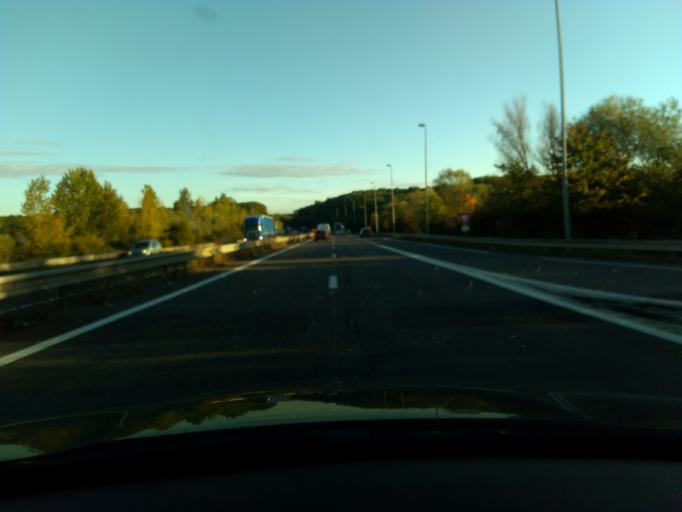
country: FR
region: Lorraine
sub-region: Departement de la Moselle
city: Peltre
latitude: 49.0957
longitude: 6.2333
